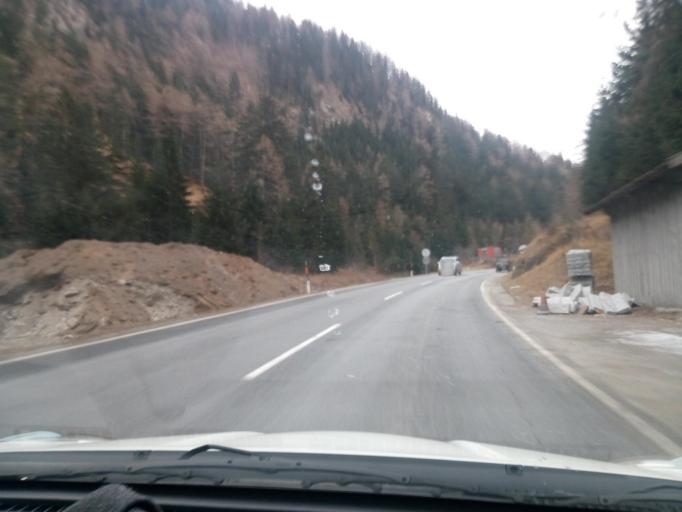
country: AT
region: Tyrol
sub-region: Politischer Bezirk Landeck
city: Nauders
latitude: 46.9097
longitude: 10.4956
